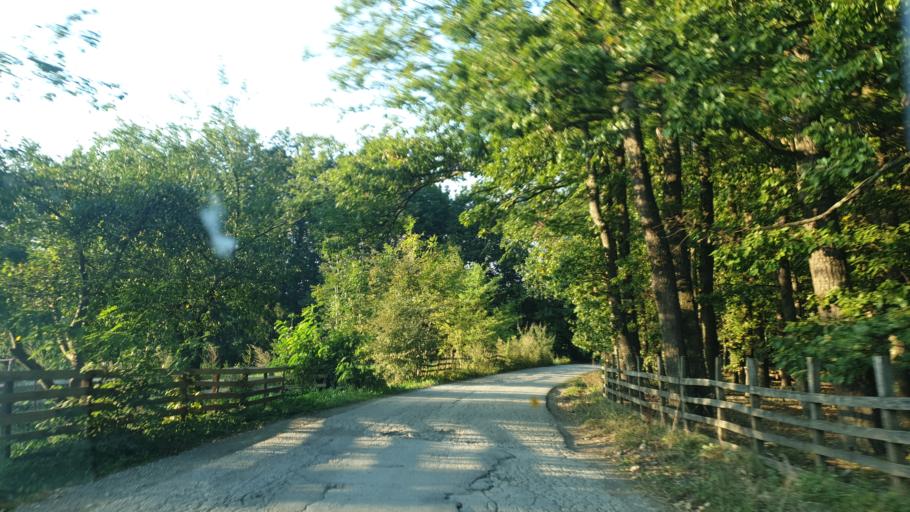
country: RS
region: Central Serbia
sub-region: Zlatiborski Okrug
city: Kosjeric
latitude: 43.9828
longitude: 20.0132
